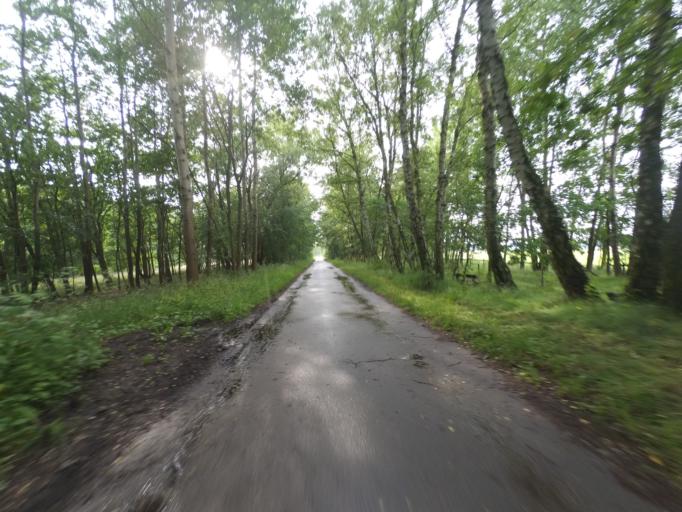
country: DE
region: Schleswig-Holstein
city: Oststeinbek
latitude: 53.5110
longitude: 10.1561
